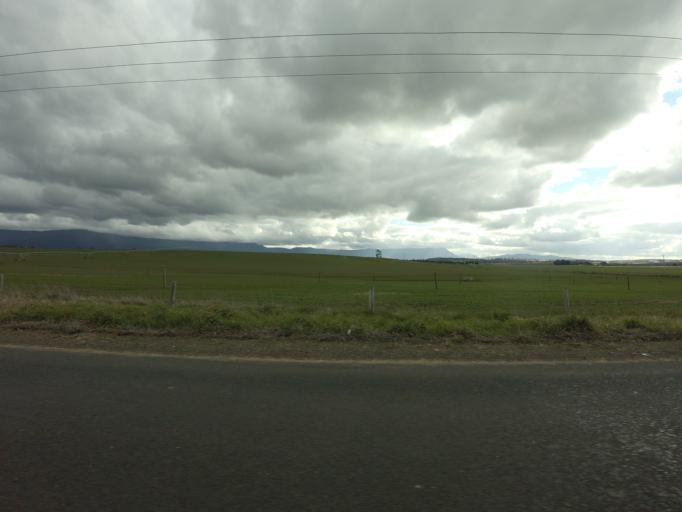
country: AU
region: Tasmania
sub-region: Northern Midlands
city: Longford
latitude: -41.7572
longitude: 147.0826
